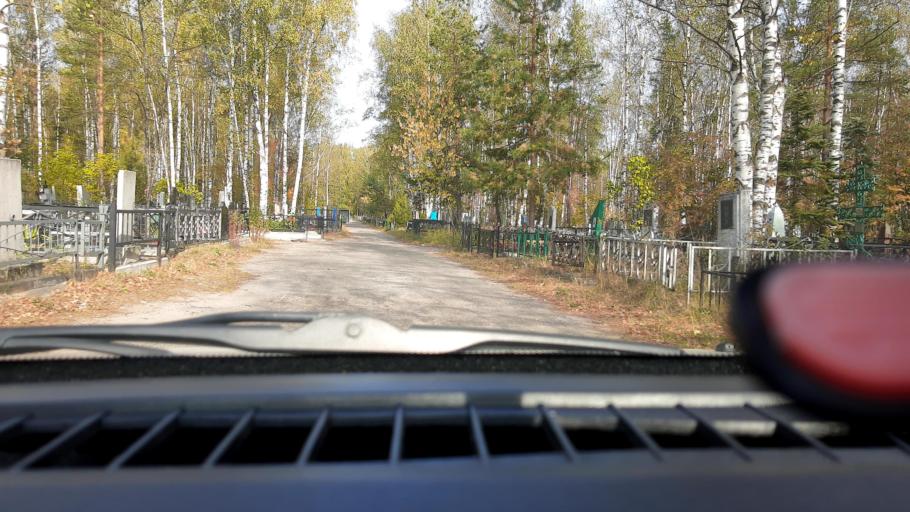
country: RU
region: Nizjnij Novgorod
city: Gorbatovka
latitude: 56.3565
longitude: 43.7838
